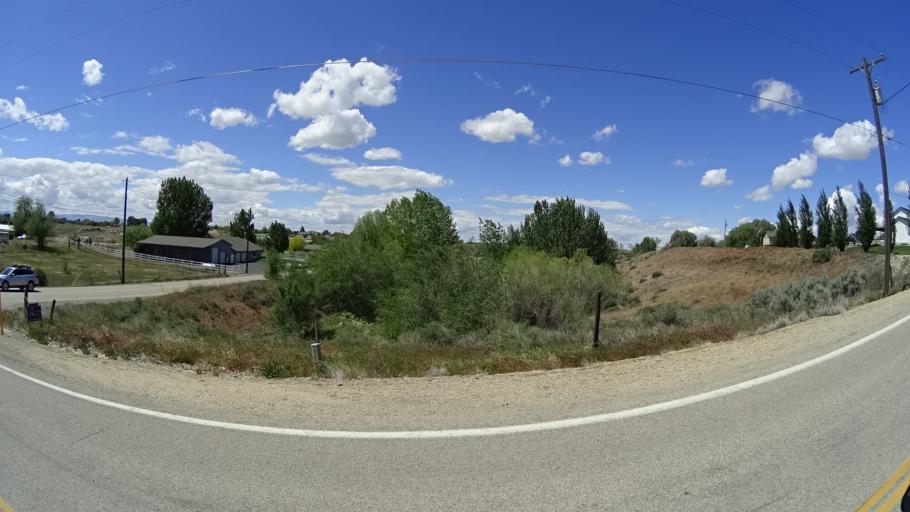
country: US
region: Idaho
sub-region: Ada County
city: Meridian
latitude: 43.5869
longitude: -116.4735
